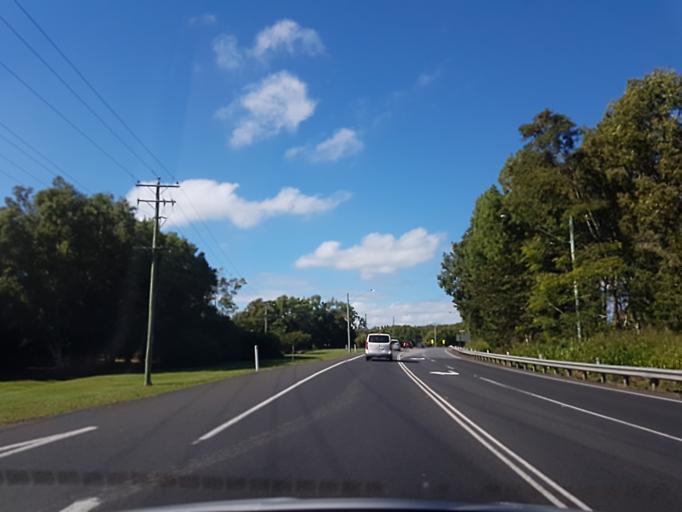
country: AU
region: Queensland
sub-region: Cairns
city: Palm Cove
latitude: -16.7724
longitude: 145.6740
